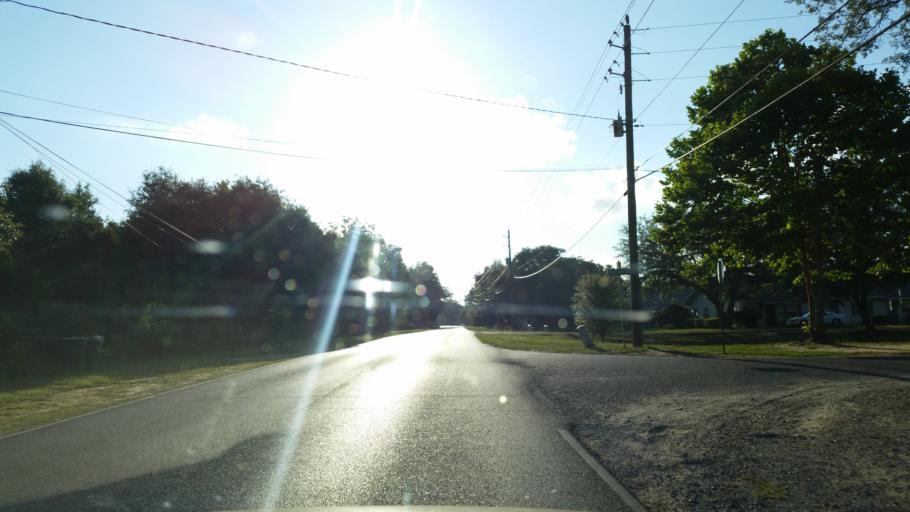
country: US
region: Florida
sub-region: Escambia County
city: Bellview
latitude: 30.4483
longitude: -87.3205
